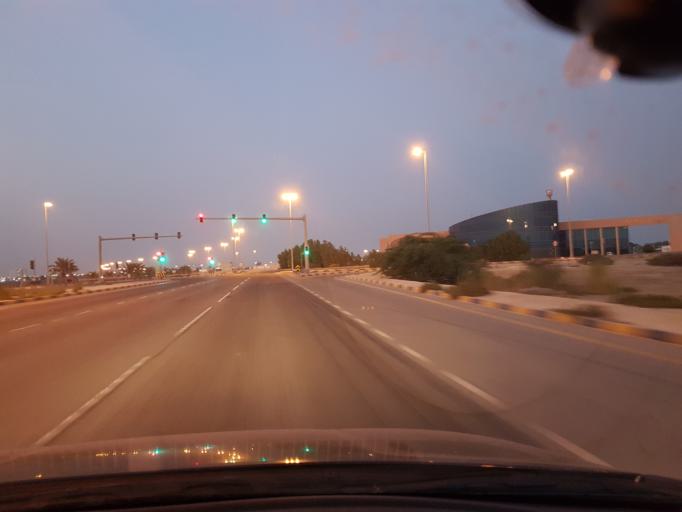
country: BH
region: Central Governorate
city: Dar Kulayb
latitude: 26.0157
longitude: 50.4859
